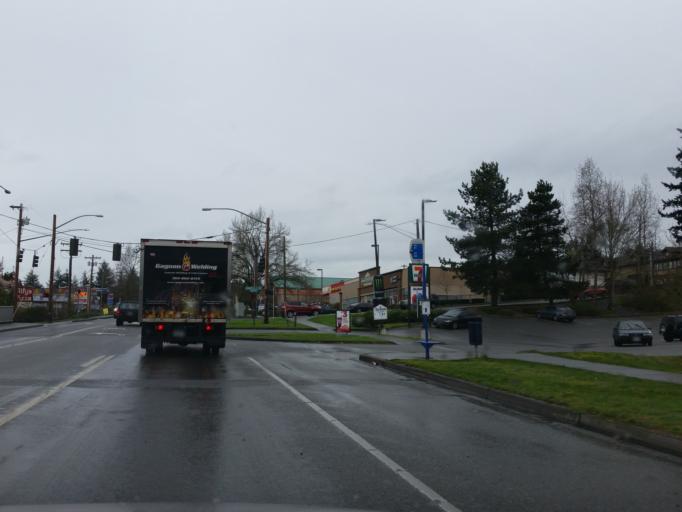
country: US
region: Washington
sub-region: Snohomish County
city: Snohomish
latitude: 47.9232
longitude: -122.0979
